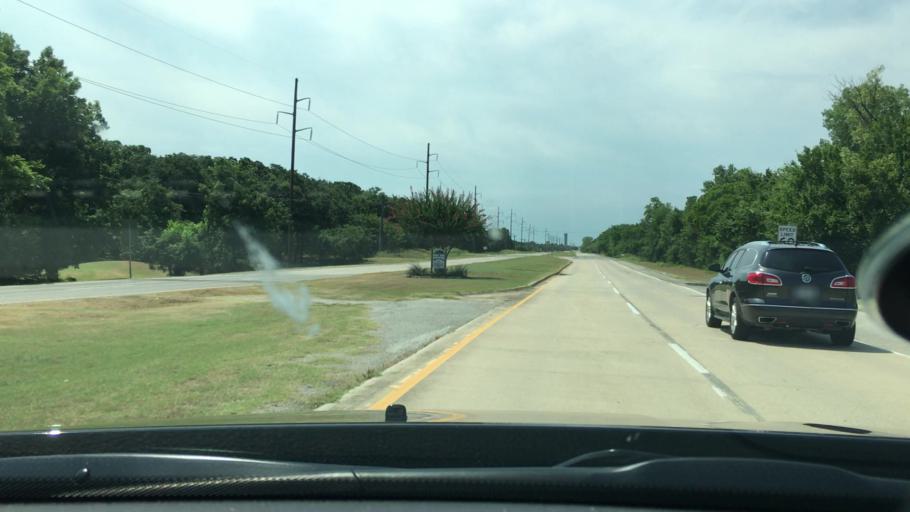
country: US
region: Oklahoma
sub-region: Carter County
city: Ardmore
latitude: 34.2186
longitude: -97.1433
